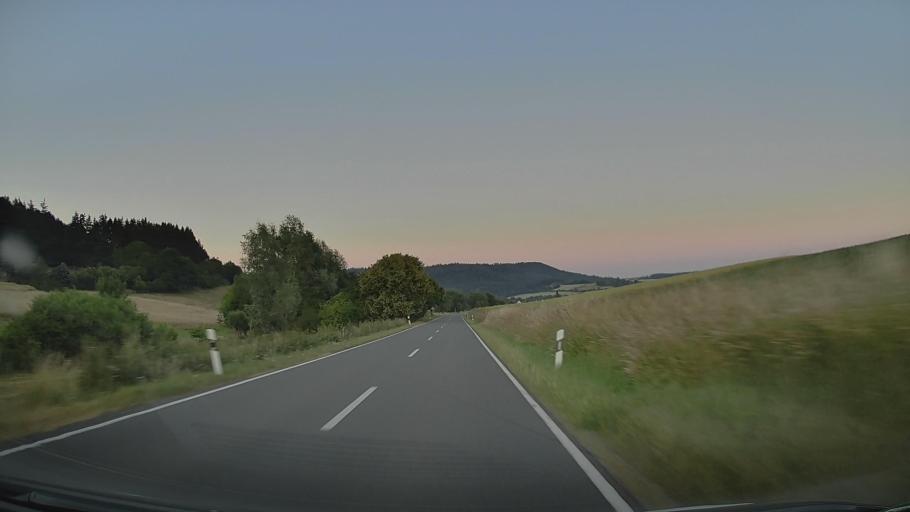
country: DE
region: Lower Saxony
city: Aerzen
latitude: 52.0140
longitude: 9.3172
